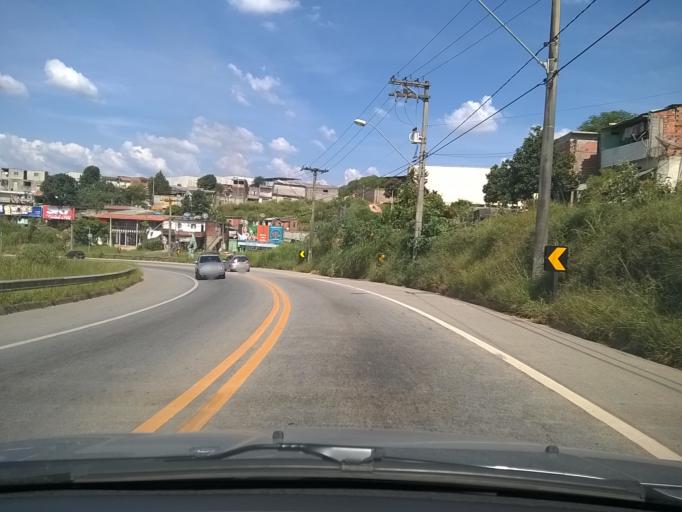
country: BR
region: Sao Paulo
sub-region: Francisco Morato
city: Francisco Morato
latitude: -23.3056
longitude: -46.7574
